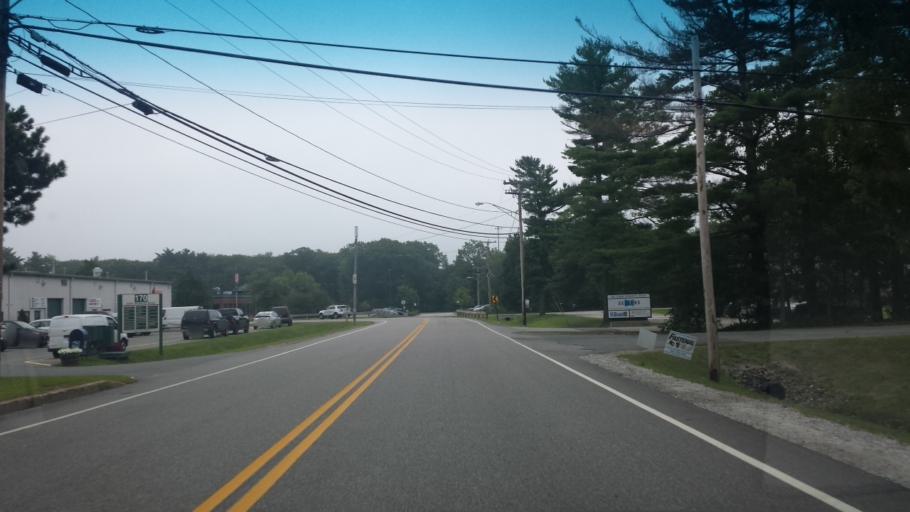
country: US
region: Maine
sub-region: Cumberland County
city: South Portland Gardens
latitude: 43.6293
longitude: -70.3277
